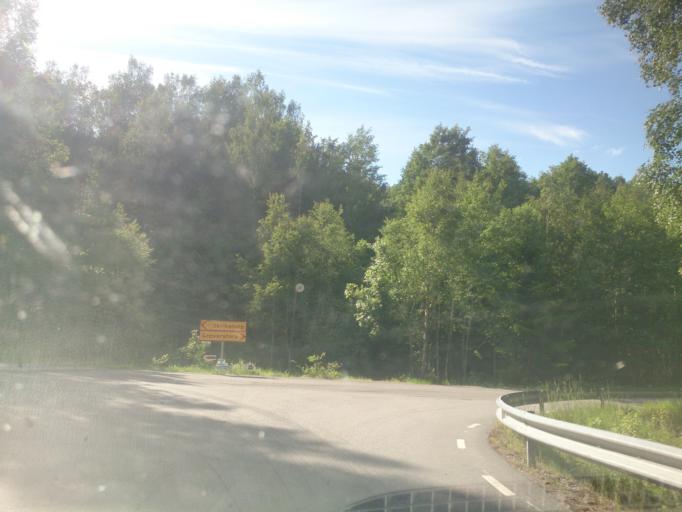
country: SE
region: OEstergoetland
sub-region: Norrkopings Kommun
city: Jursla
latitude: 58.6864
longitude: 16.1502
